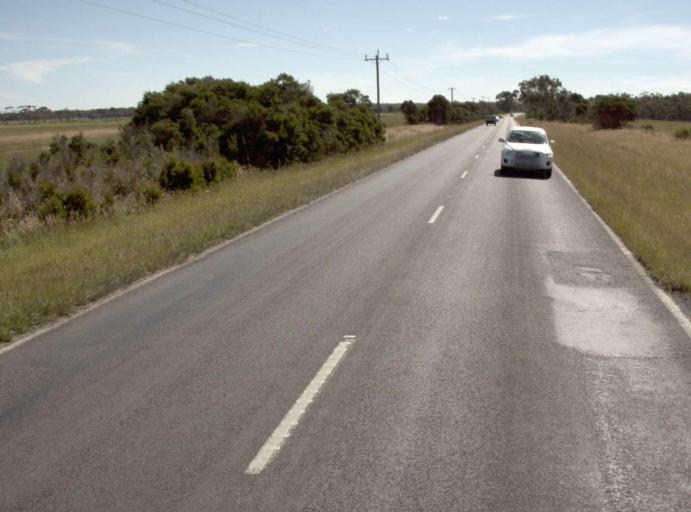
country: AU
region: Victoria
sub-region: Latrobe
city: Morwell
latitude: -38.6345
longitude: 146.5391
